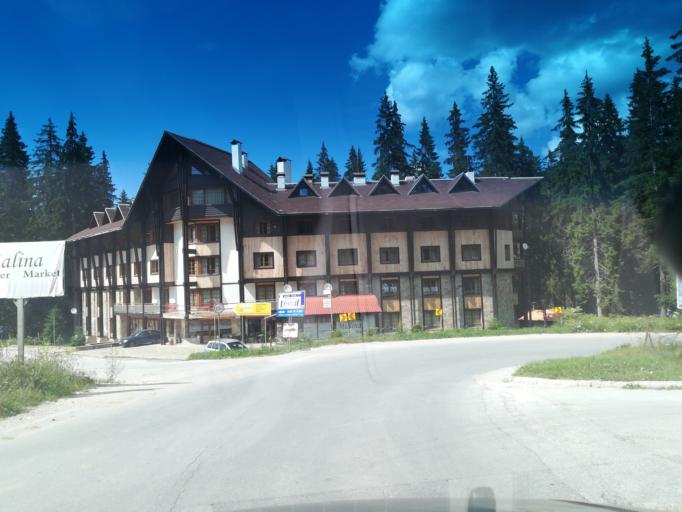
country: BG
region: Smolyan
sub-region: Obshtina Smolyan
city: Smolyan
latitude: 41.6535
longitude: 24.6848
